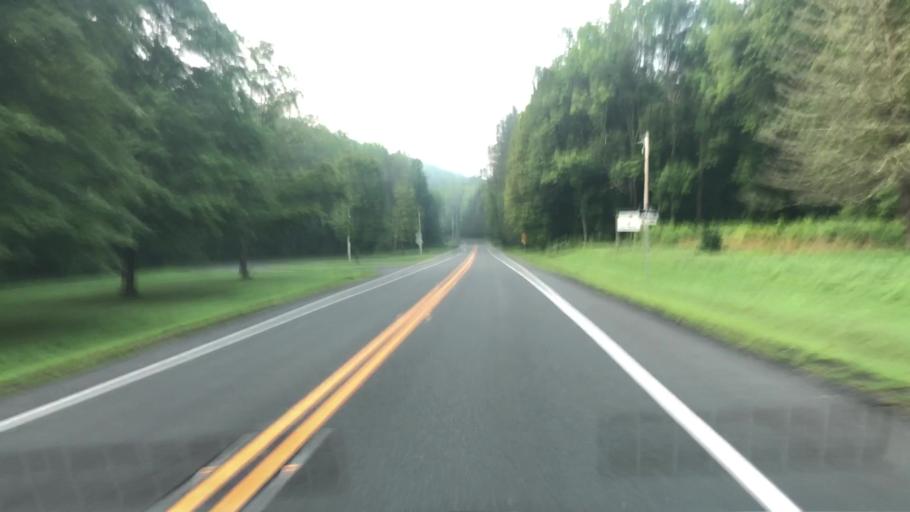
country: US
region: Massachusetts
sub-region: Franklin County
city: Buckland
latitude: 42.5638
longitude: -72.8040
